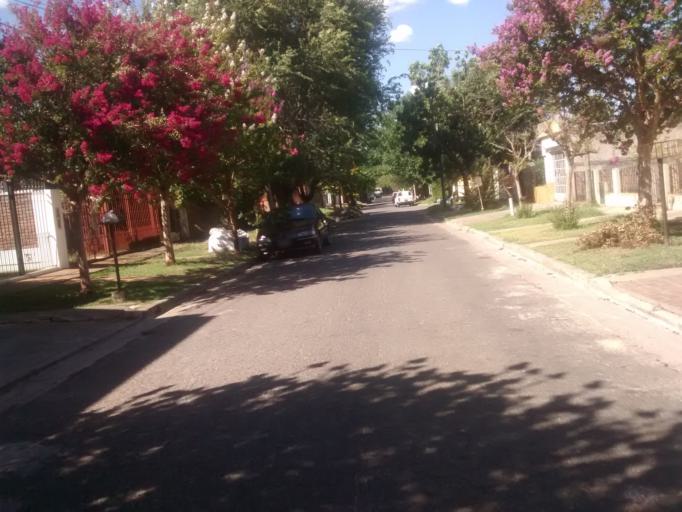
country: AR
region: Buenos Aires
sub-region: Partido de La Plata
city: La Plata
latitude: -34.9319
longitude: -57.9031
